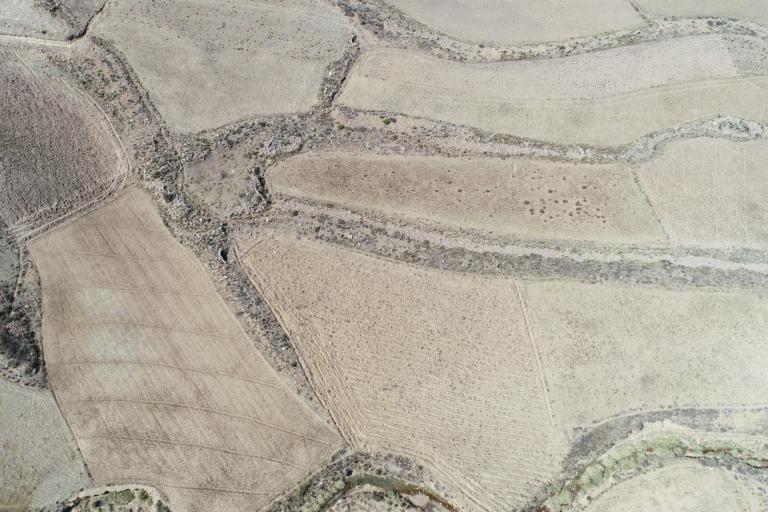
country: BO
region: La Paz
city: Achacachi
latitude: -15.8888
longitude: -68.8107
